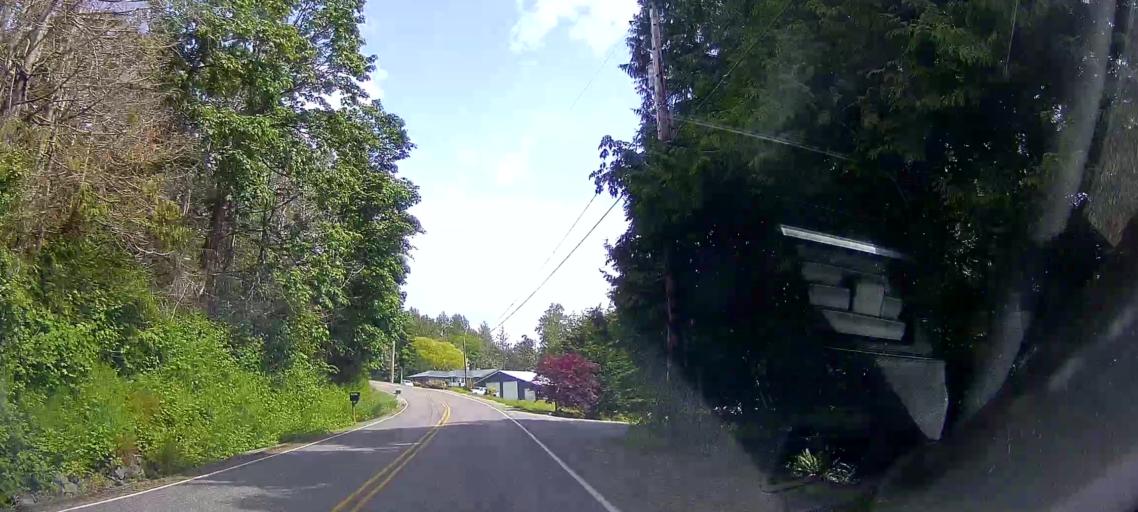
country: US
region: Washington
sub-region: Skagit County
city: Burlington
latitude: 48.5723
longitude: -122.3963
